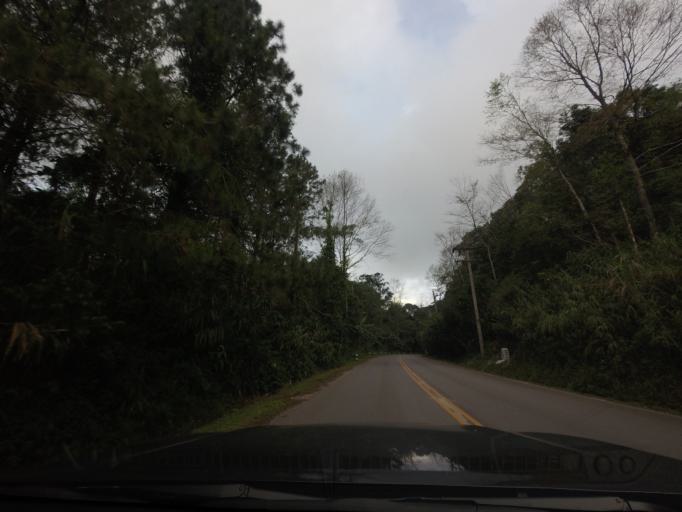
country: TH
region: Phetchabun
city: Lom Kao
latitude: 16.8937
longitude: 101.0983
